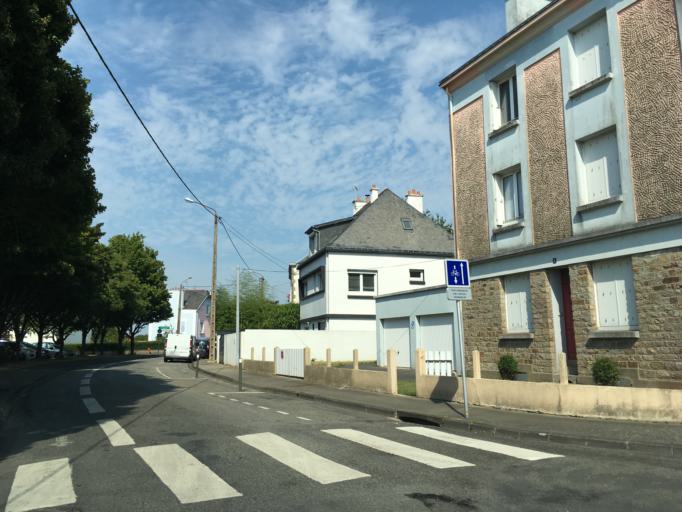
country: FR
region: Brittany
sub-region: Departement du Morbihan
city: Lorient
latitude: 47.7603
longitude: -3.3810
